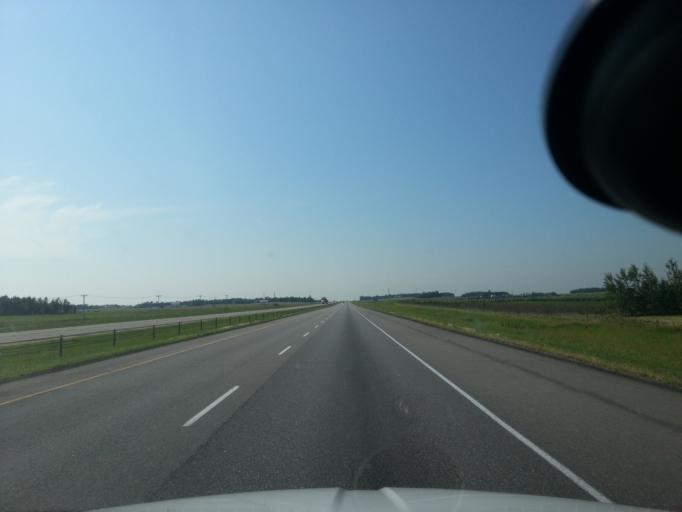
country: CA
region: Alberta
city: Olds
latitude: 51.9007
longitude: -114.0256
